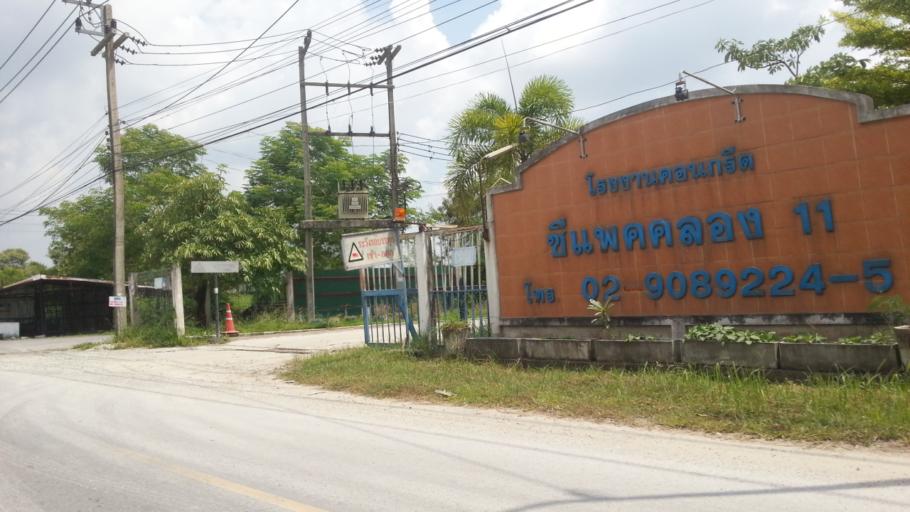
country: TH
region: Pathum Thani
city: Ban Rangsit
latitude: 14.0475
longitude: 100.8115
